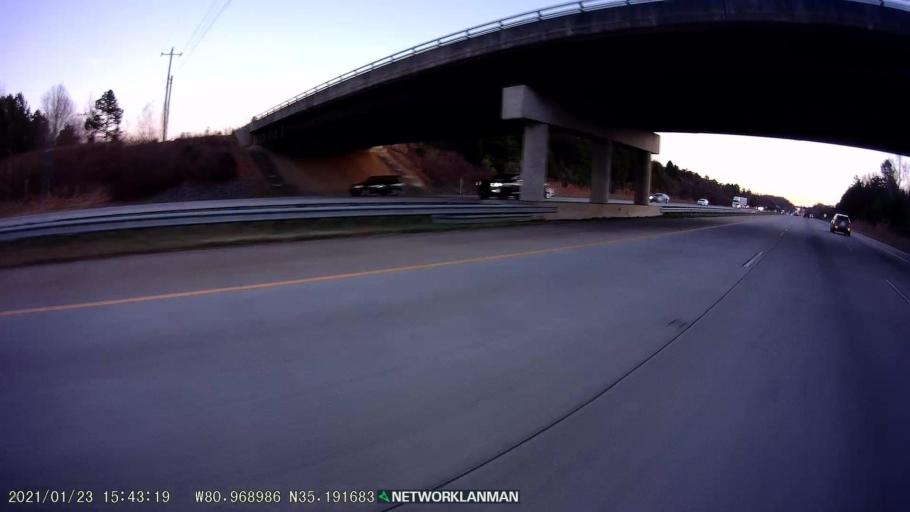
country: US
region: North Carolina
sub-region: Gaston County
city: Belmont
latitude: 35.1917
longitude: -80.9697
